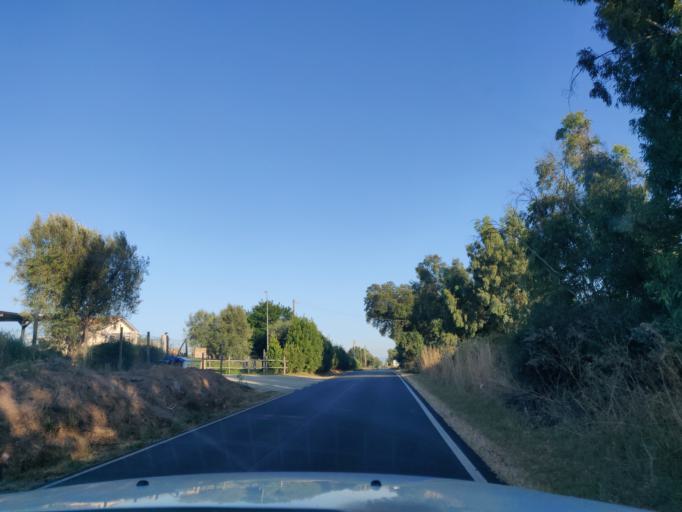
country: IT
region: Latium
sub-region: Provincia di Viterbo
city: Montalto di Castro
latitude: 42.2931
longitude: 11.6541
